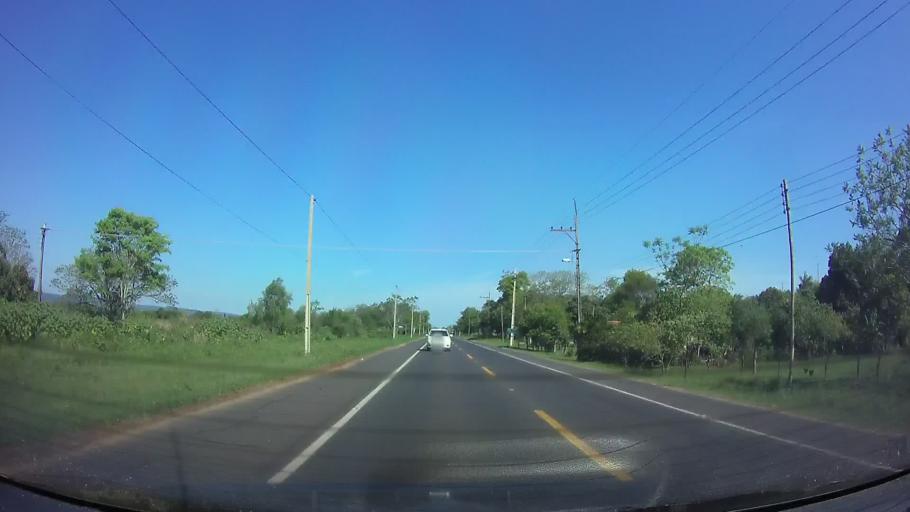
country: PY
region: Central
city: Ypacarai
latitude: -25.3856
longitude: -57.2985
